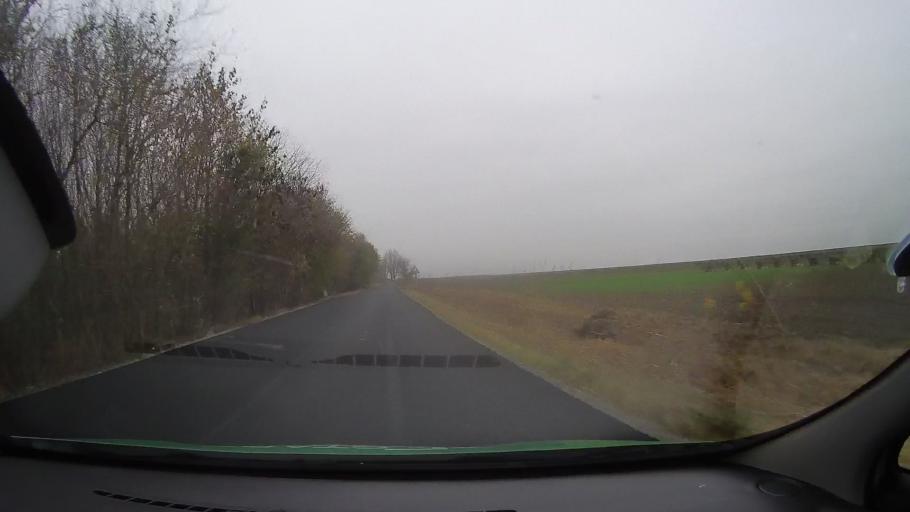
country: RO
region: Ialomita
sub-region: Comuna Valea Ciorii
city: Valea Ciorii
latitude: 44.7449
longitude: 27.5734
